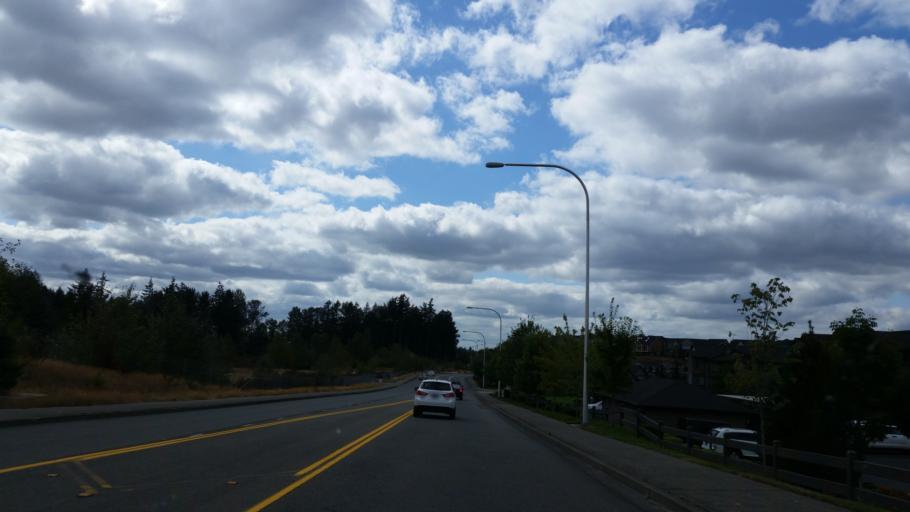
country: US
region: Washington
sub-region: King County
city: Pacific
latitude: 47.2466
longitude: -122.1992
